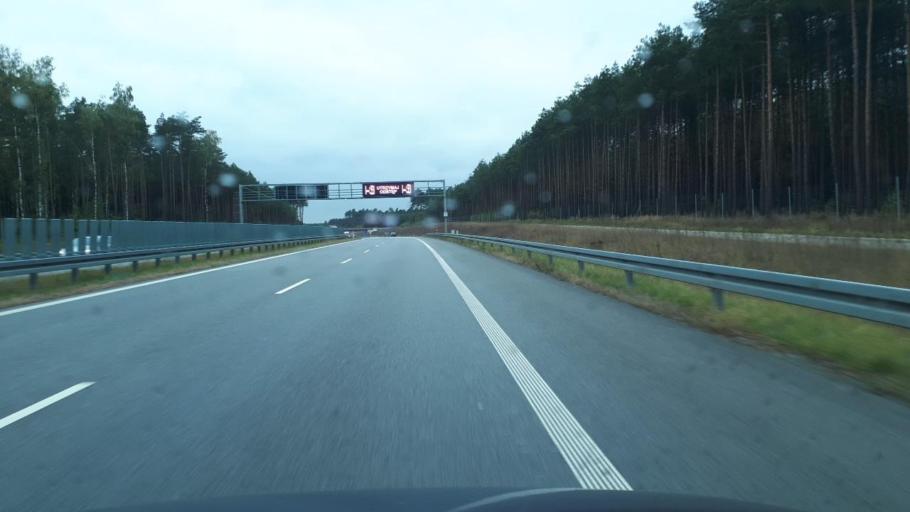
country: PL
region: Greater Poland Voivodeship
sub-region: Powiat kepinski
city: Kepno
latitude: 51.3283
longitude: 17.9833
